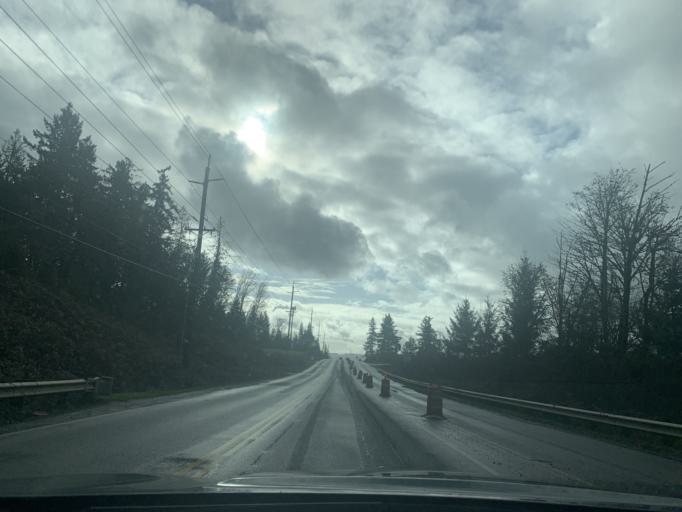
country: US
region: Oregon
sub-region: Washington County
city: King City
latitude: 45.4069
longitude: -122.8516
